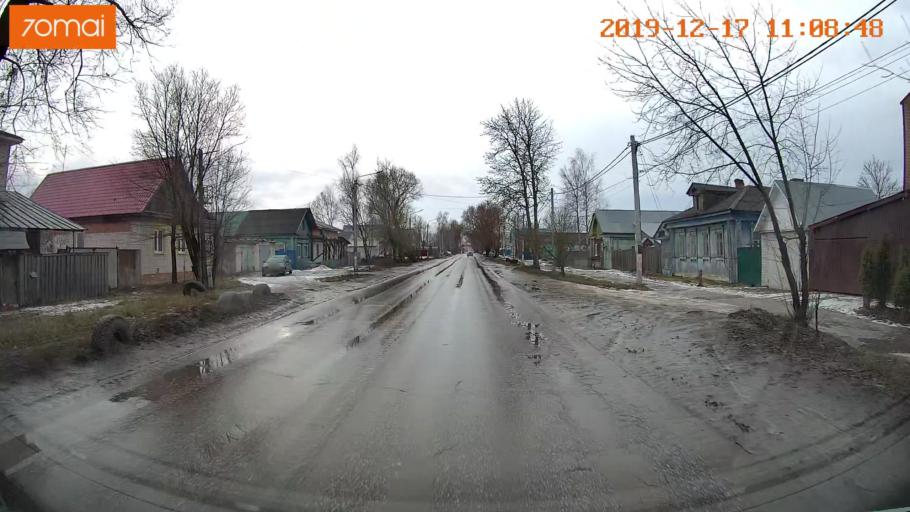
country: RU
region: Vladimir
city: Gus'-Khrustal'nyy
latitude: 55.6056
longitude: 40.6431
